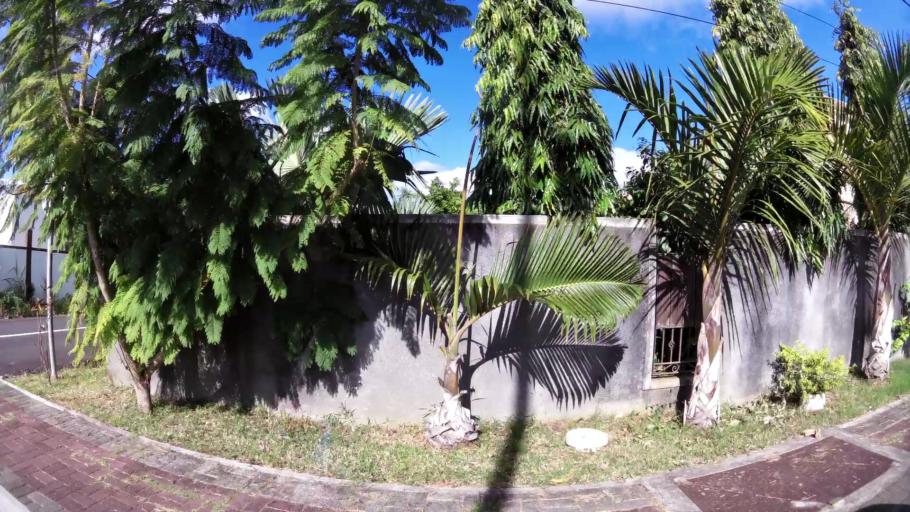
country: MU
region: Plaines Wilhems
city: Quatre Bornes
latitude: -20.2699
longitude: 57.4871
